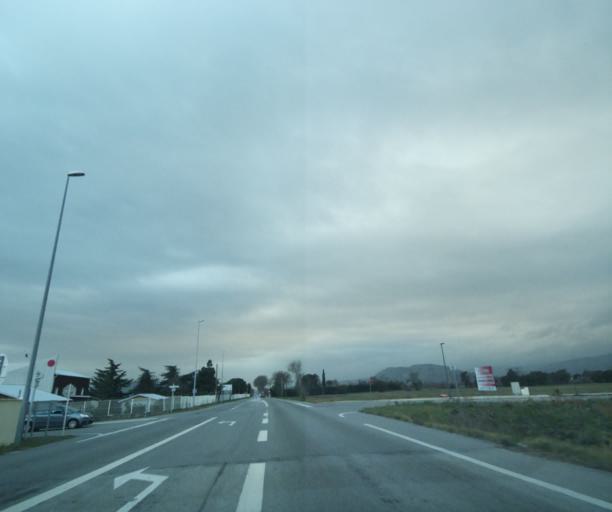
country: FR
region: Rhone-Alpes
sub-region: Departement de la Drome
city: Bourg-les-Valence
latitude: 44.9731
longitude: 4.8958
